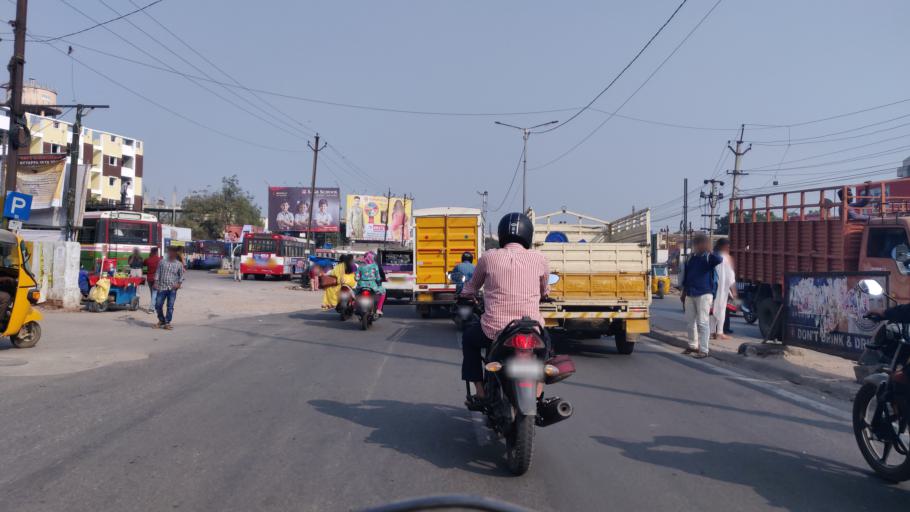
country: IN
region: Telangana
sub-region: Rangareddi
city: Uppal Kalan
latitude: 17.4015
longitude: 78.5681
